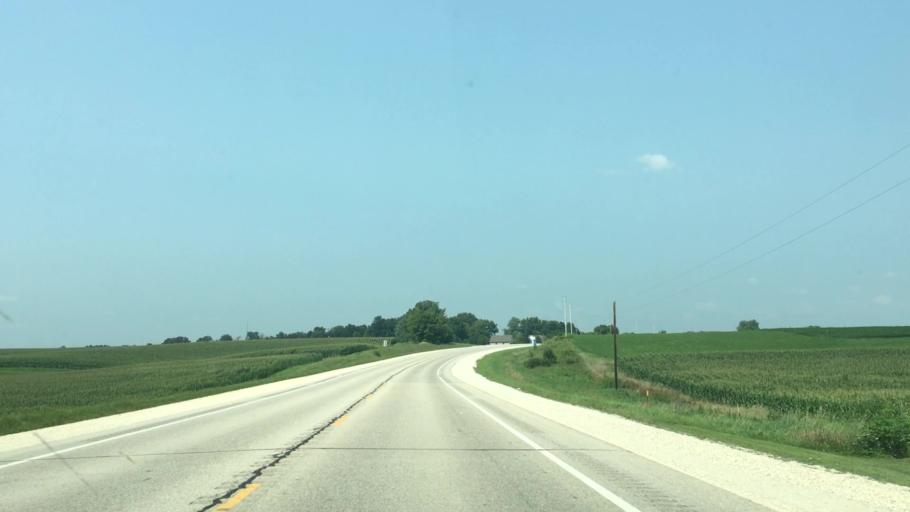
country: US
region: Iowa
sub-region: Winneshiek County
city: Decorah
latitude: 43.2589
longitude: -91.8381
